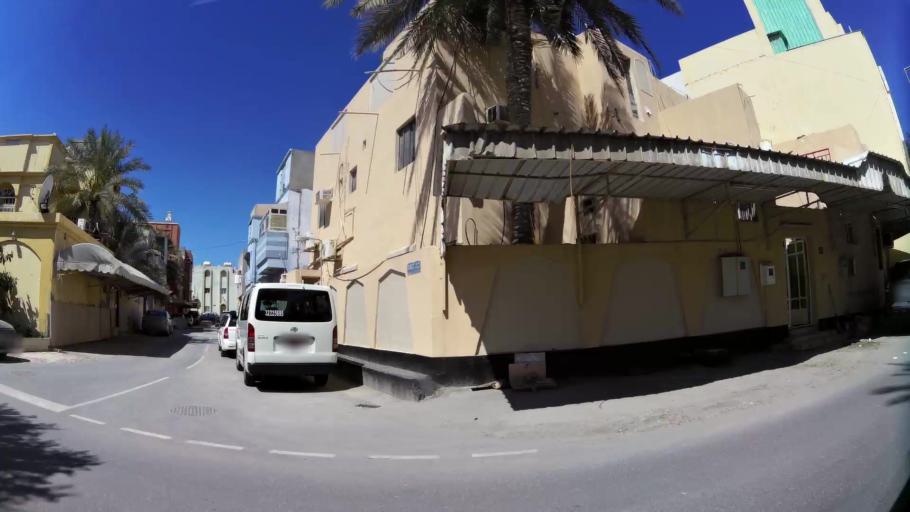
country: BH
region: Muharraq
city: Al Muharraq
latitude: 26.2782
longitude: 50.6357
